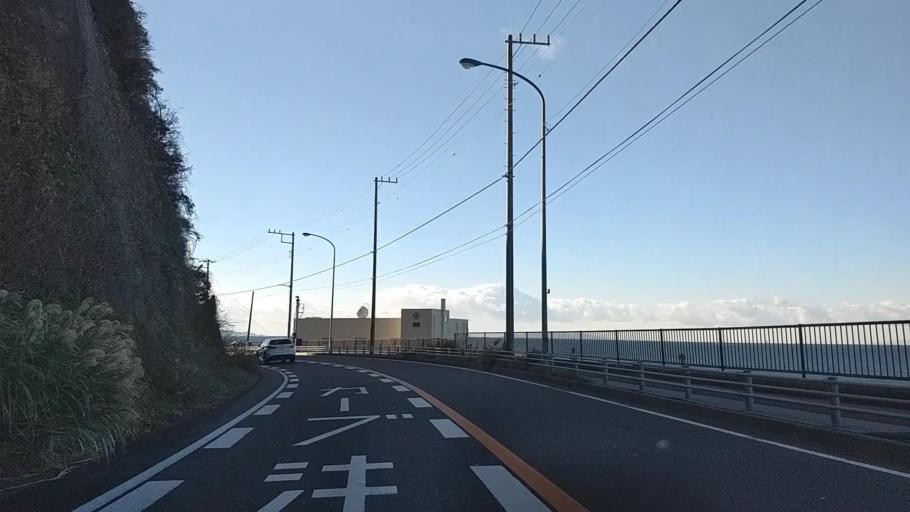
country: JP
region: Chiba
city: Futtsu
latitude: 35.1579
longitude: 139.8192
